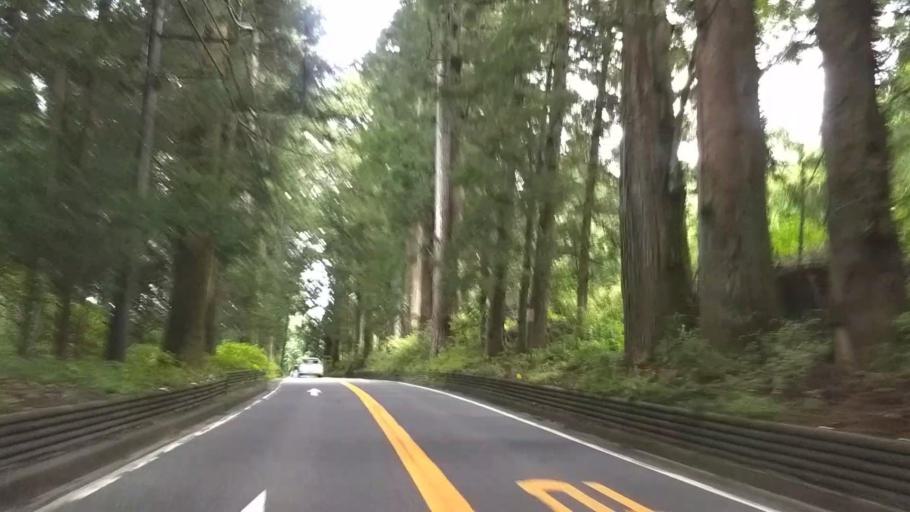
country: JP
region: Tochigi
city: Nikko
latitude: 36.7369
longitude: 139.6422
